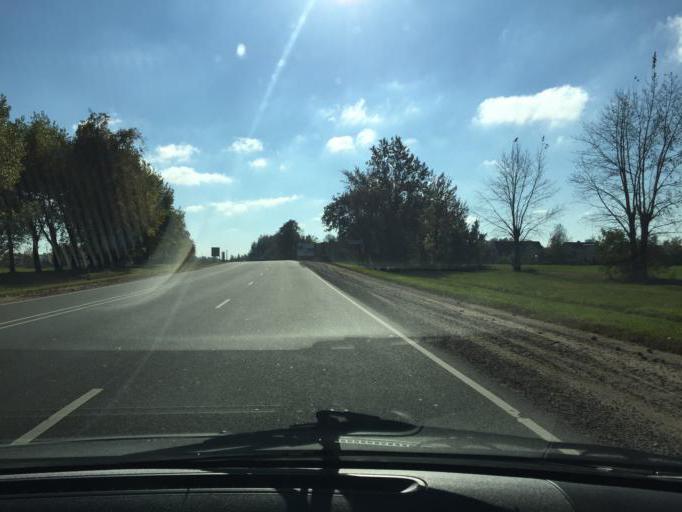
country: BY
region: Minsk
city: Slutsk
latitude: 53.0570
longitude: 27.5535
